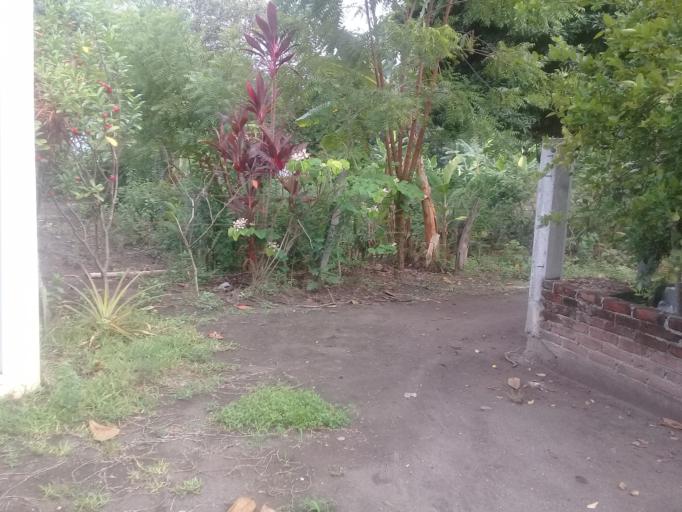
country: MX
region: Veracruz
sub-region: Paso de Ovejas
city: Tolome
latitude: 19.2631
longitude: -96.4132
